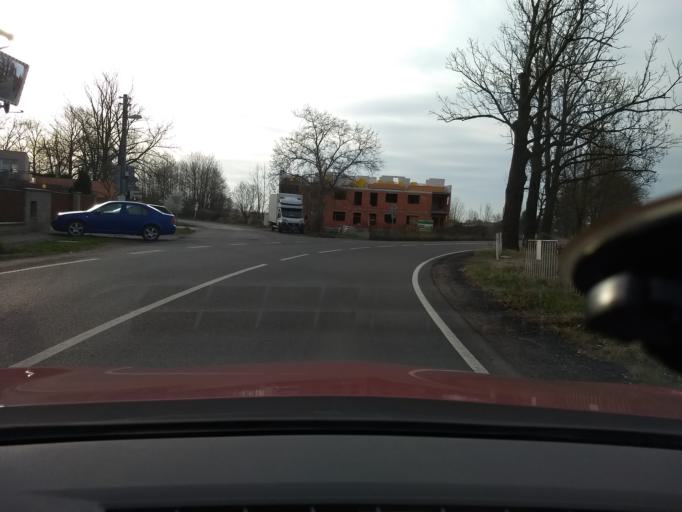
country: CZ
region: Central Bohemia
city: Jenec
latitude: 50.0509
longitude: 14.1791
